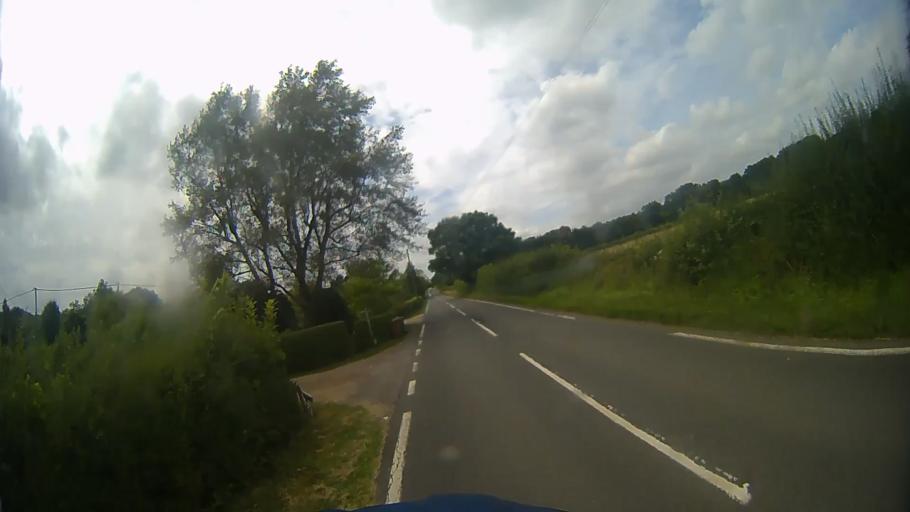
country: GB
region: England
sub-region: Hampshire
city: Kingsley
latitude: 51.1695
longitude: -0.8613
